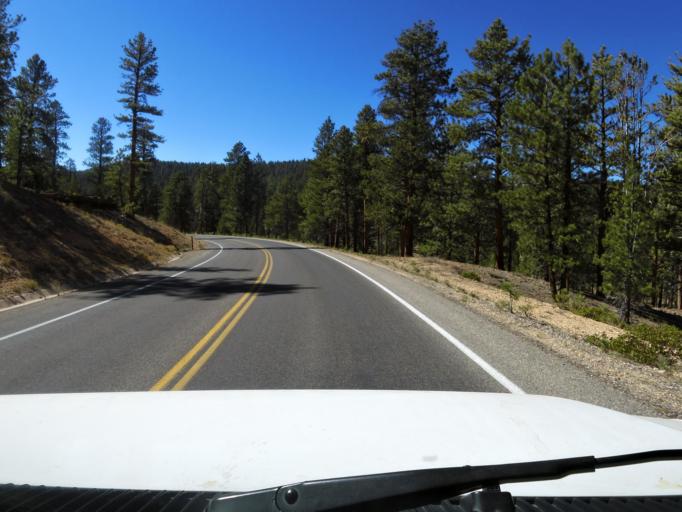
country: US
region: Utah
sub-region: Garfield County
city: Panguitch
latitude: 37.6057
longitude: -112.2045
